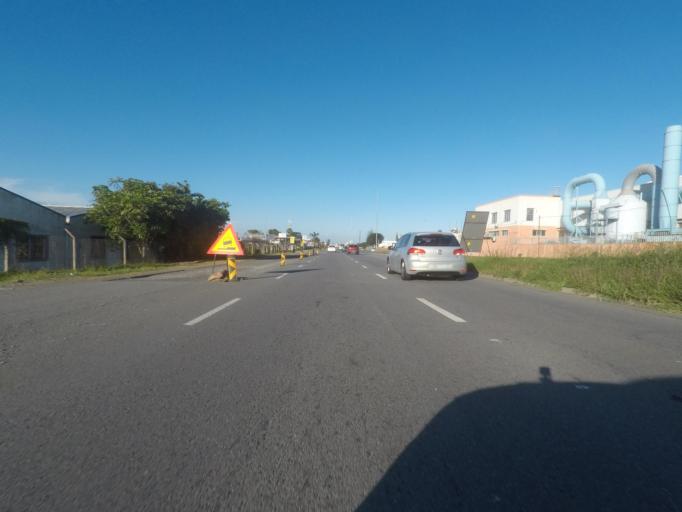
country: ZA
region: Eastern Cape
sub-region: Buffalo City Metropolitan Municipality
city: East London
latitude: -33.0329
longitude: 27.8833
